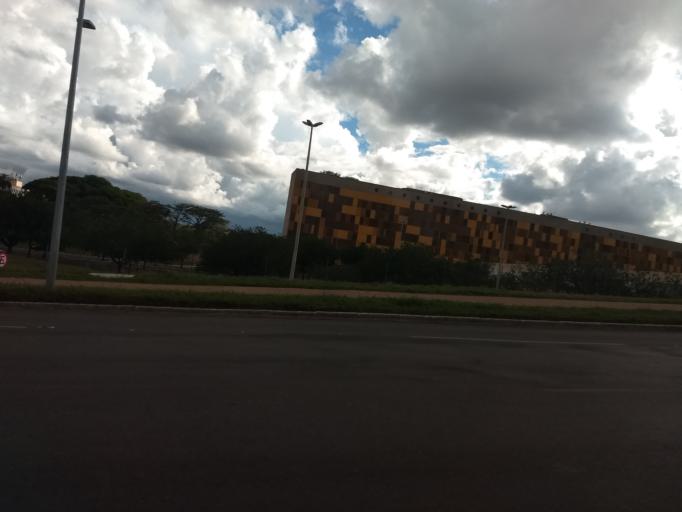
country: BR
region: Federal District
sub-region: Brasilia
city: Brasilia
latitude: -15.8008
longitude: -47.8636
